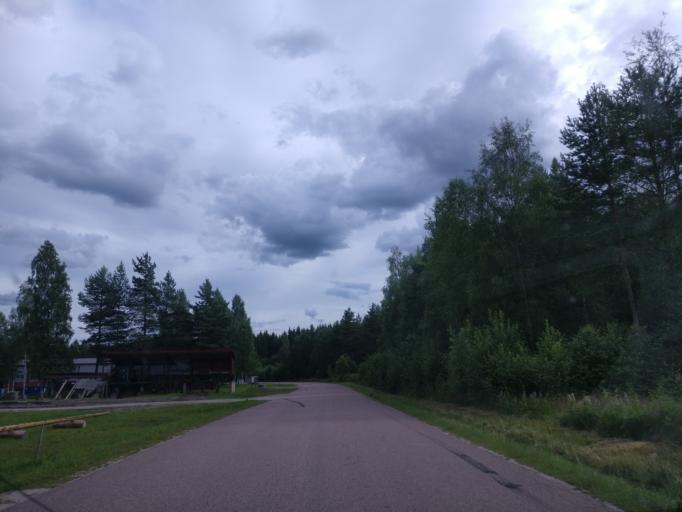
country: SE
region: Vaermland
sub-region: Hagfors Kommun
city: Ekshaerad
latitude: 60.1640
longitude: 13.4981
